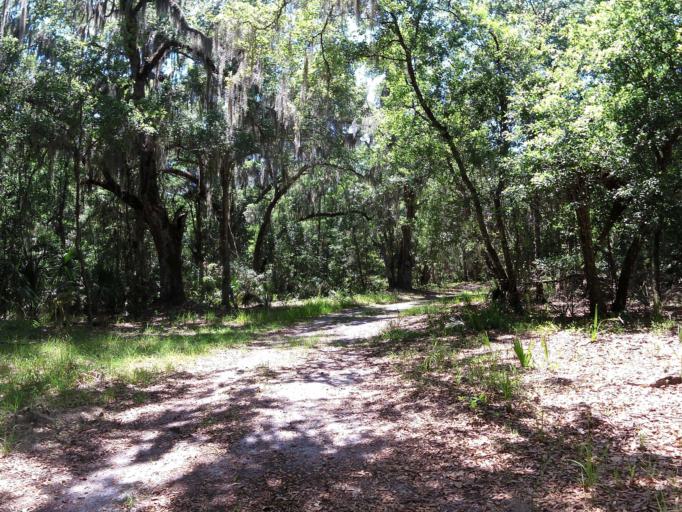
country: US
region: Florida
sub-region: Duval County
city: Atlantic Beach
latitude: 30.4431
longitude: -81.4674
